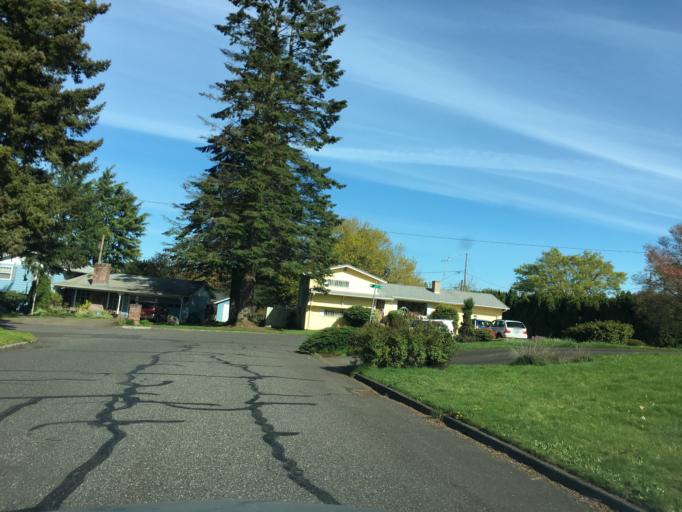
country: US
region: Oregon
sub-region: Multnomah County
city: Lents
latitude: 45.5445
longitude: -122.5327
